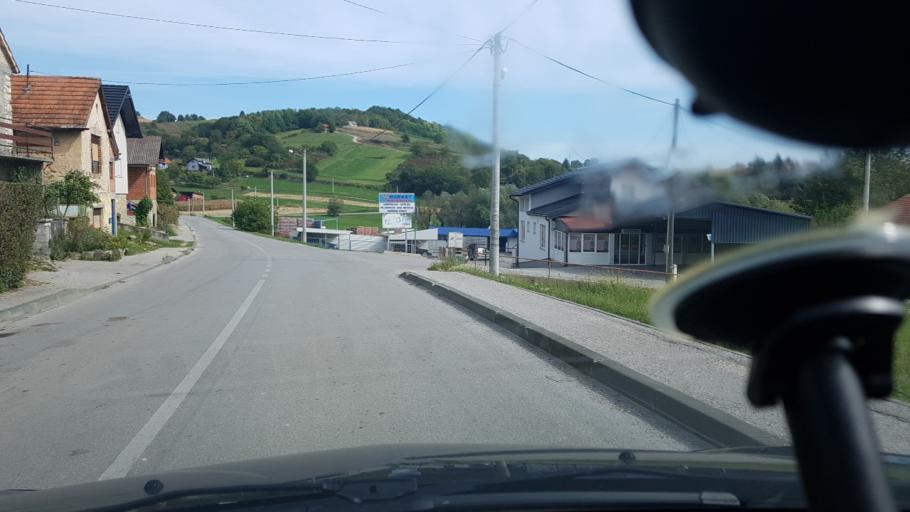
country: HR
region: Varazdinska
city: Ljubescica
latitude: 46.0922
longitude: 16.3289
